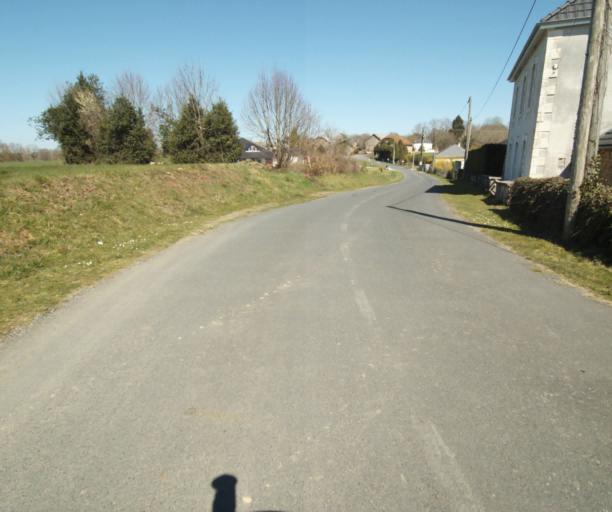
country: FR
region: Limousin
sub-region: Departement de la Correze
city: Saint-Clement
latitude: 45.2988
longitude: 1.6910
